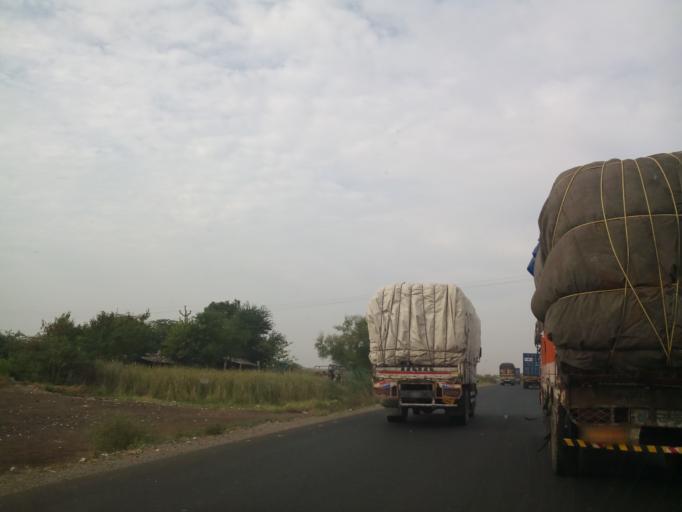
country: IN
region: Gujarat
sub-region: Ahmadabad
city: Dhandhuka
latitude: 22.5900
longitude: 72.0674
